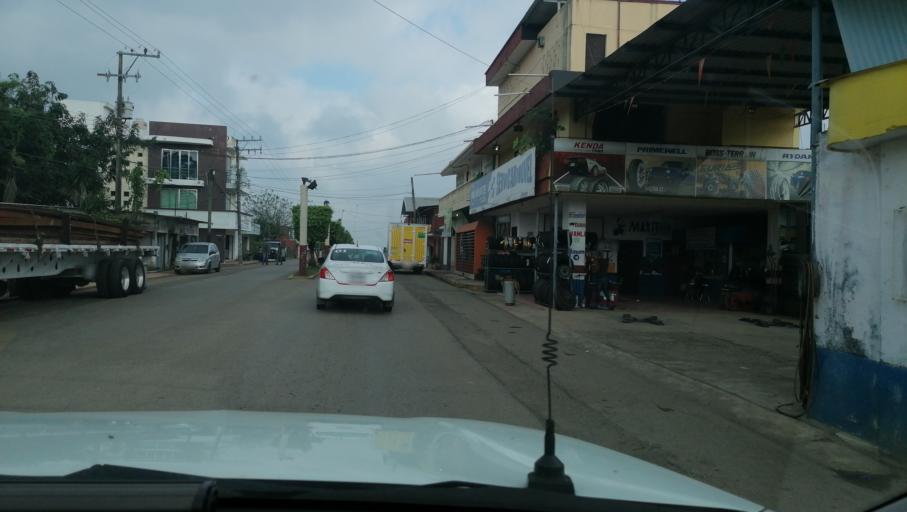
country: MX
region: Chiapas
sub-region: Juarez
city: El Triunfo 1ra. Seccion (Cardona)
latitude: 17.6047
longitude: -93.1884
